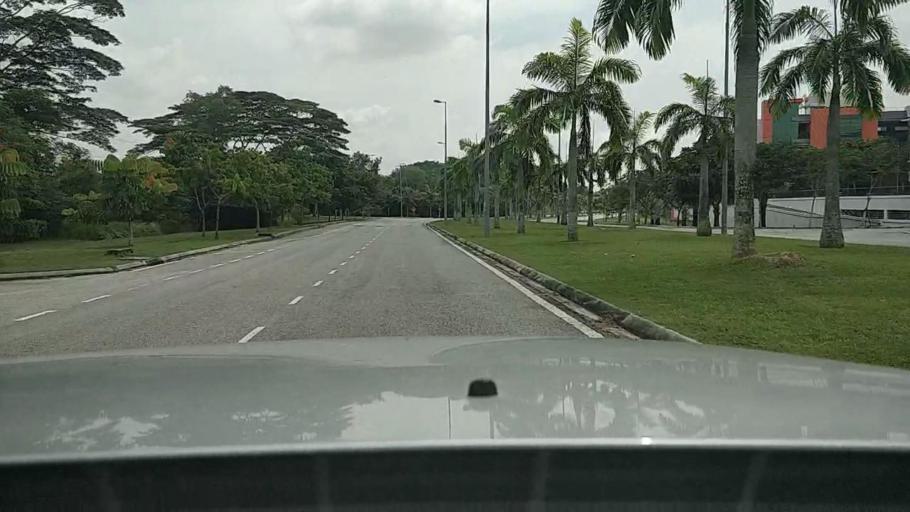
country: MY
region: Putrajaya
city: Putrajaya
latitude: 2.9059
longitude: 101.6521
